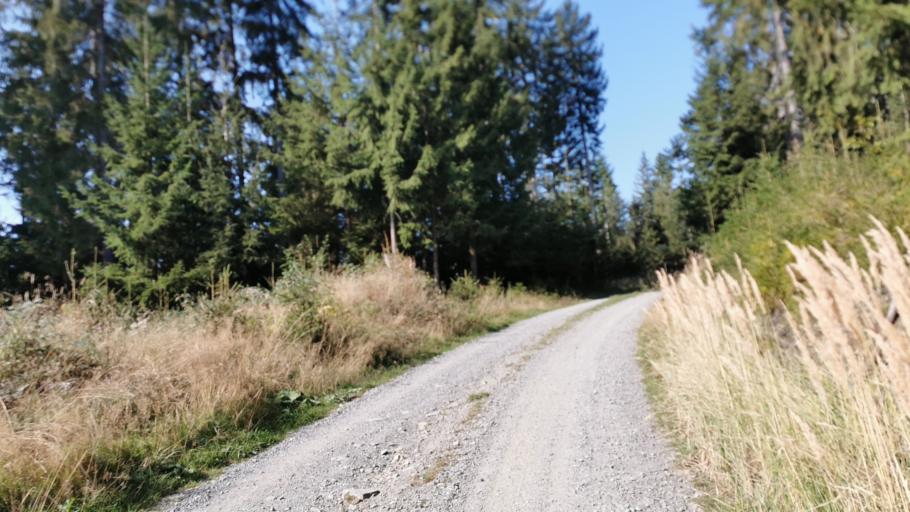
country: DE
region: Bavaria
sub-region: Upper Franconia
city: Tschirn
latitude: 50.4160
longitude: 11.4387
